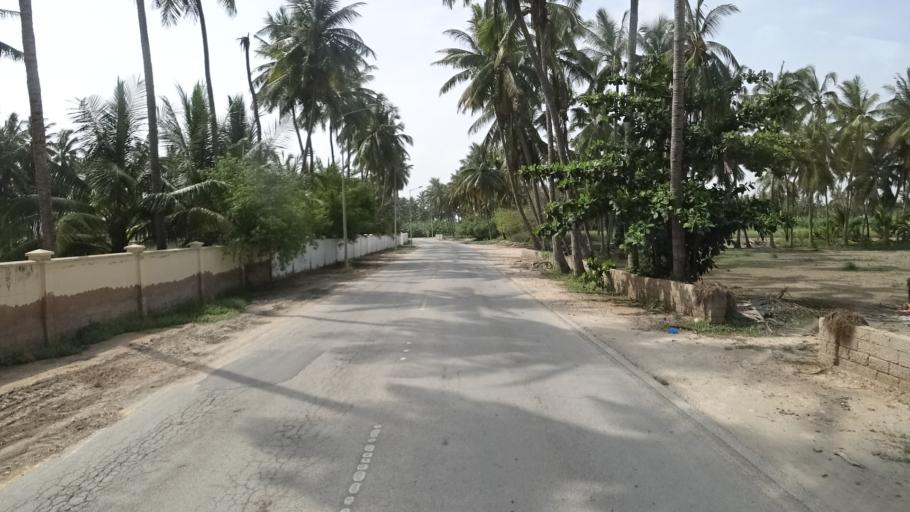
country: OM
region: Zufar
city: Salalah
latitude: 17.0138
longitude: 54.1529
